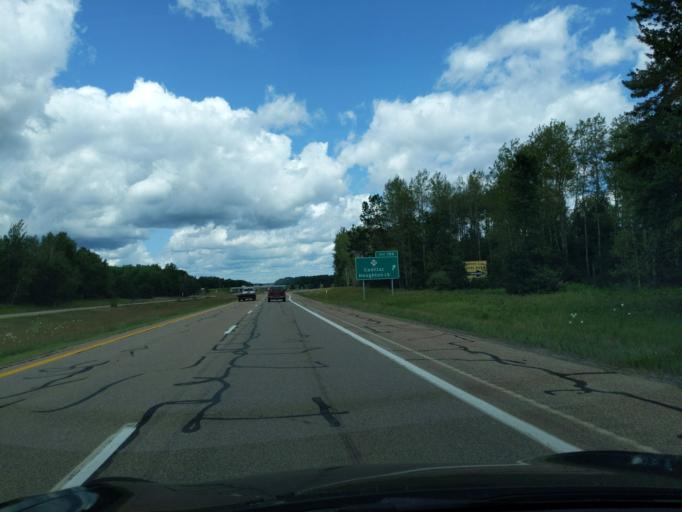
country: US
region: Michigan
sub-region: Roscommon County
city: Houghton Lake
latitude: 44.3293
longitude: -84.8071
